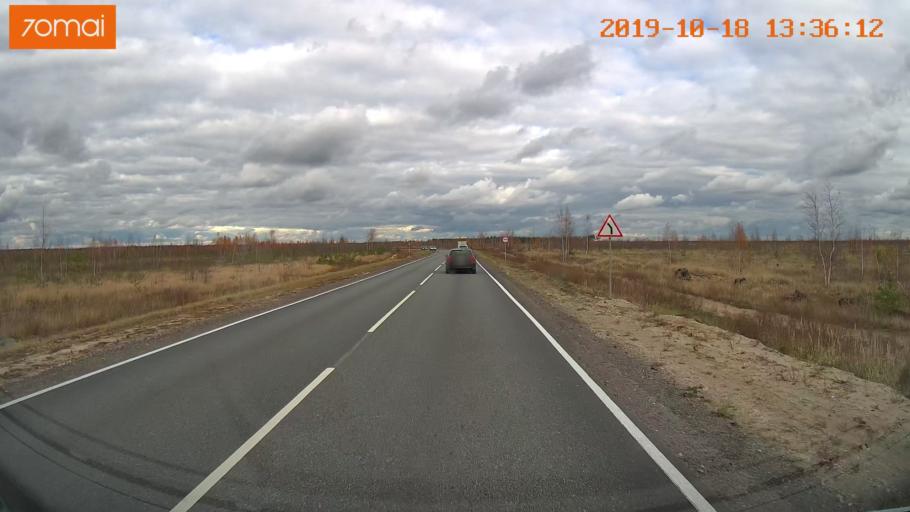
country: RU
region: Rjazan
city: Solotcha
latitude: 54.8678
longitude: 39.9821
